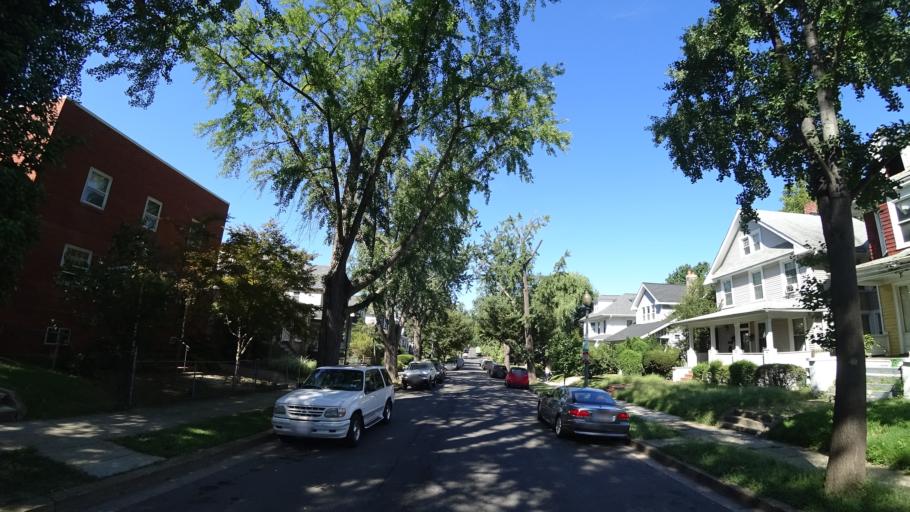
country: US
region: Maryland
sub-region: Montgomery County
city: Takoma Park
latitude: 38.9490
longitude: -77.0280
